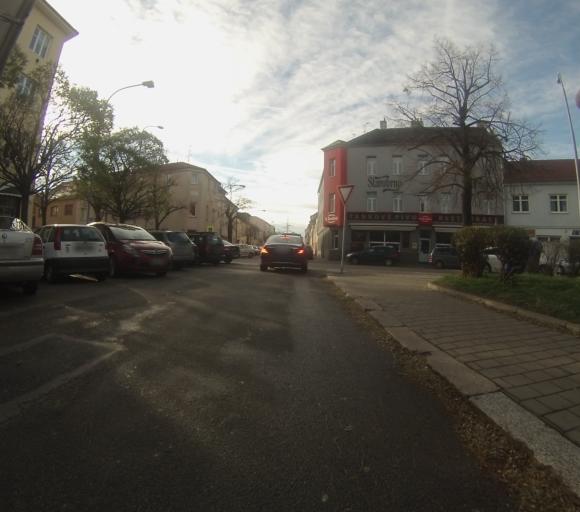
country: CZ
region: South Moravian
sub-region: Mesto Brno
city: Brno
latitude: 49.1994
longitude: 16.6320
